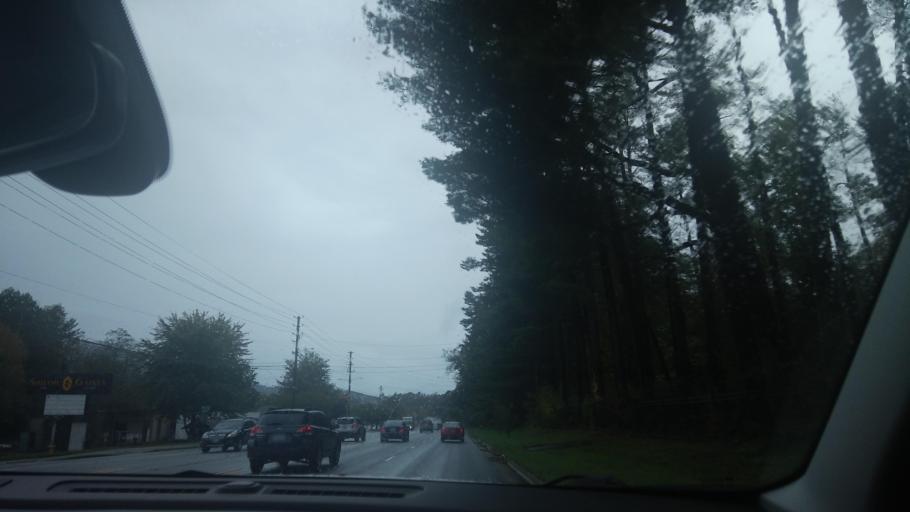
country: US
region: North Carolina
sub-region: Buncombe County
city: Biltmore Forest
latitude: 35.5474
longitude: -82.5346
